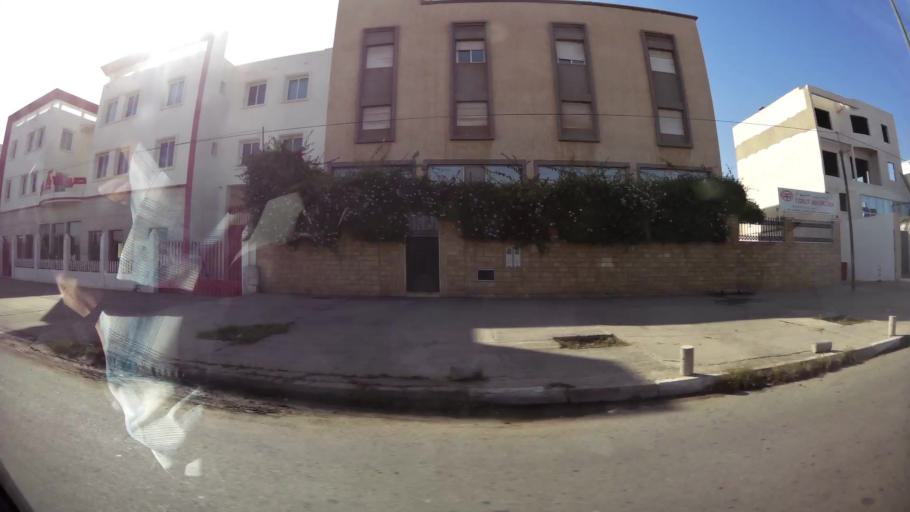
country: MA
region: Souss-Massa-Draa
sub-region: Inezgane-Ait Mellou
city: Inezgane
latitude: 30.3861
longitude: -9.5160
